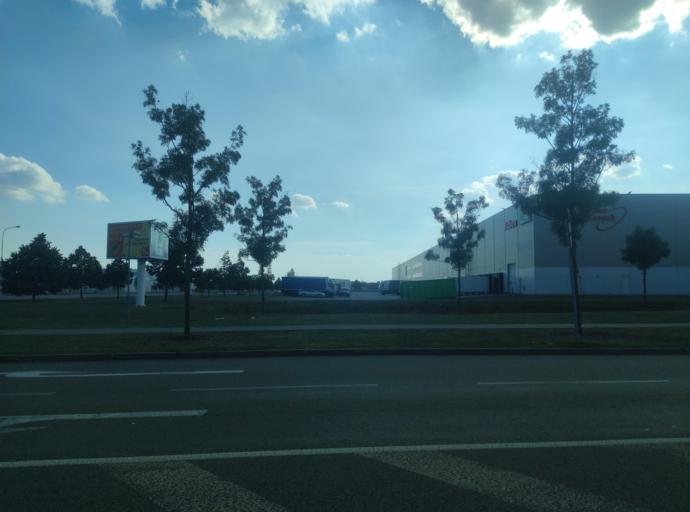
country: CZ
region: South Moravian
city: Podoli
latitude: 49.1755
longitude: 16.6688
